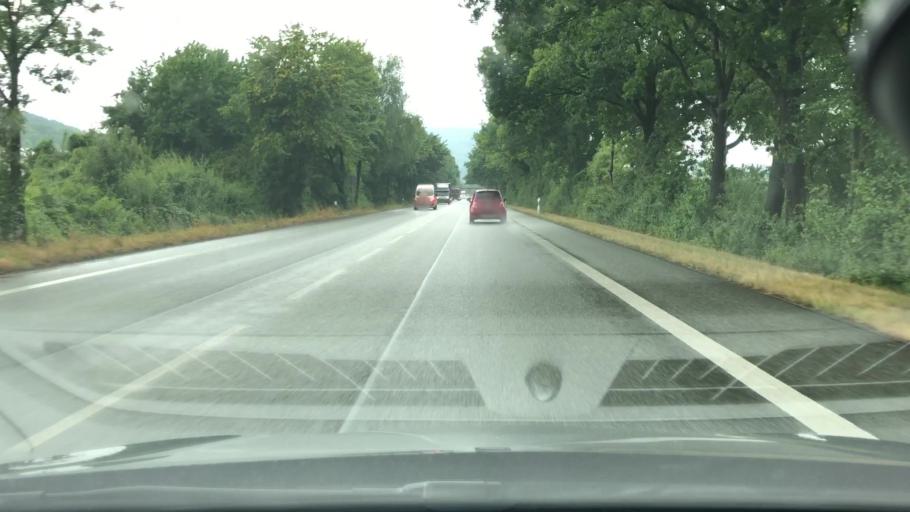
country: DE
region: North Rhine-Westphalia
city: Porta Westfalica
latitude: 52.2540
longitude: 8.9382
